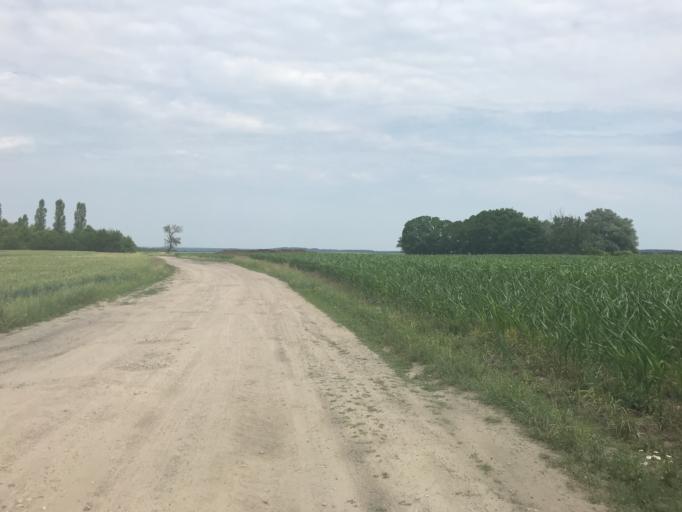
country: PL
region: West Pomeranian Voivodeship
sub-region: Powiat gryfinski
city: Chojna
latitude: 52.9200
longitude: 14.4360
